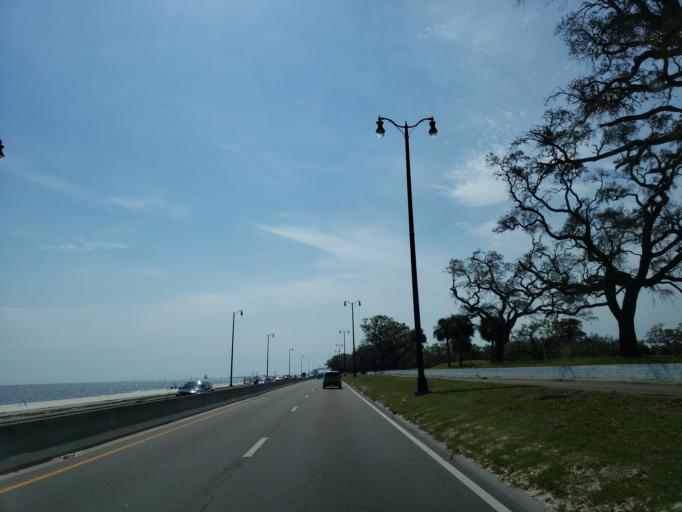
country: US
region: Mississippi
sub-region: Harrison County
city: Gulfport
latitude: 30.3869
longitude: -89.0077
